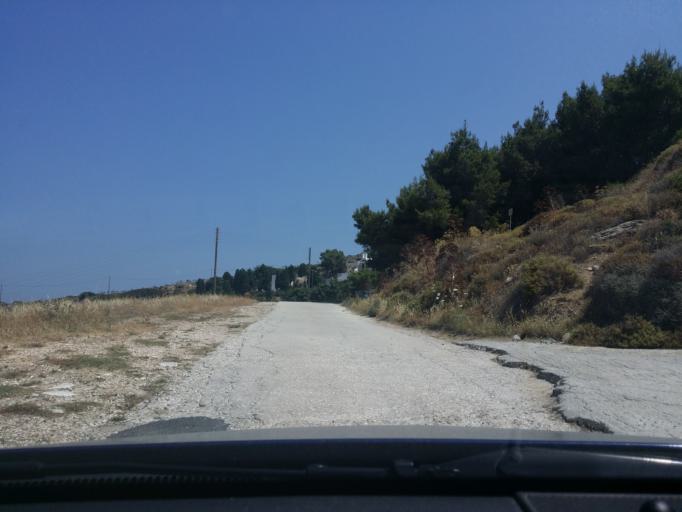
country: GR
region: South Aegean
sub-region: Nomos Kykladon
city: Paros
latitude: 37.0509
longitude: 25.1300
